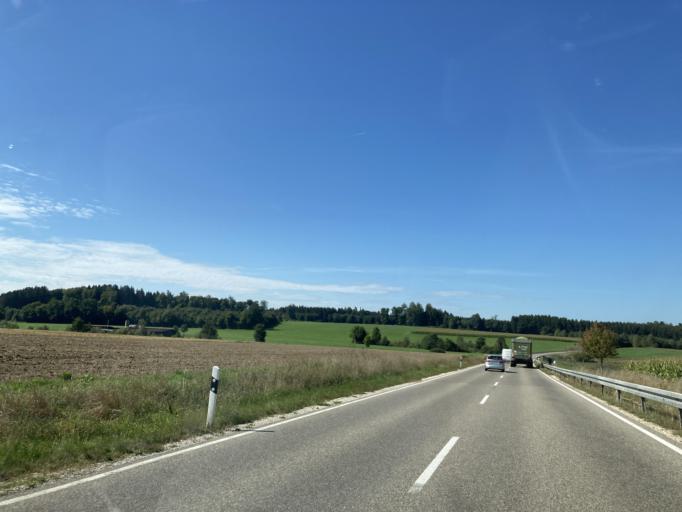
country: DE
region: Baden-Wuerttemberg
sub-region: Tuebingen Region
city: Uttenweiler
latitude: 48.1429
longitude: 9.6017
